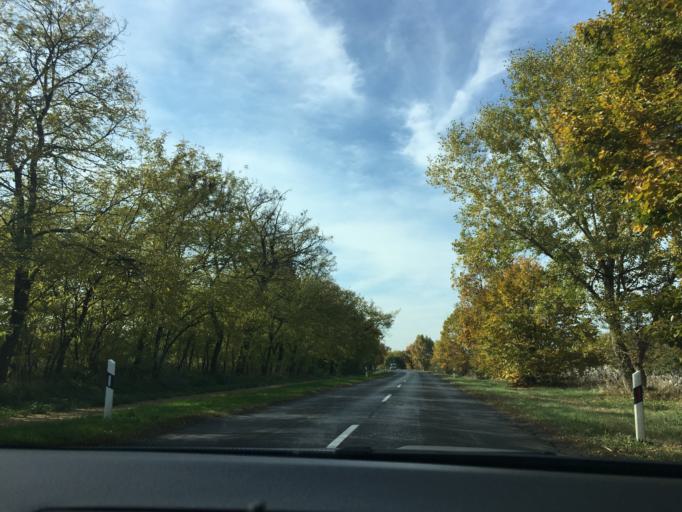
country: HU
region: Hajdu-Bihar
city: Vamospercs
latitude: 47.5268
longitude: 21.9290
